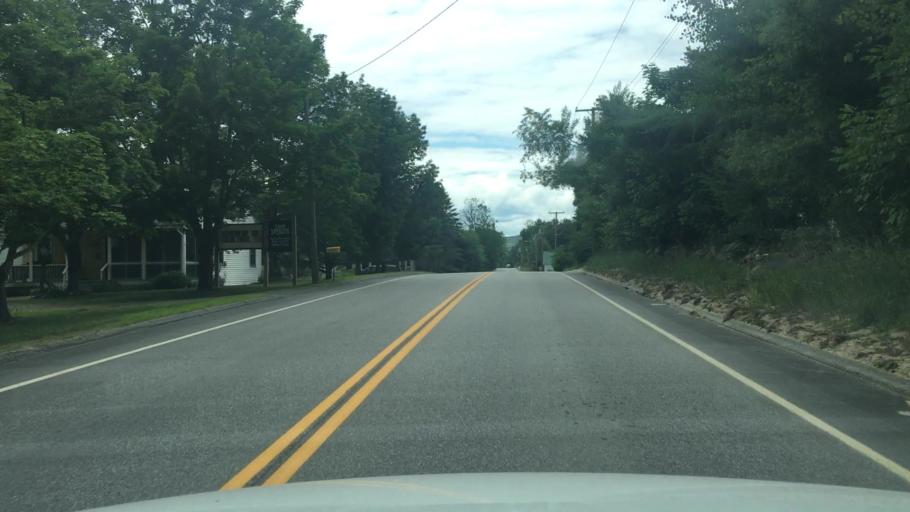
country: US
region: Maine
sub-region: Oxford County
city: Hartford
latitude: 44.3665
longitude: -70.4605
